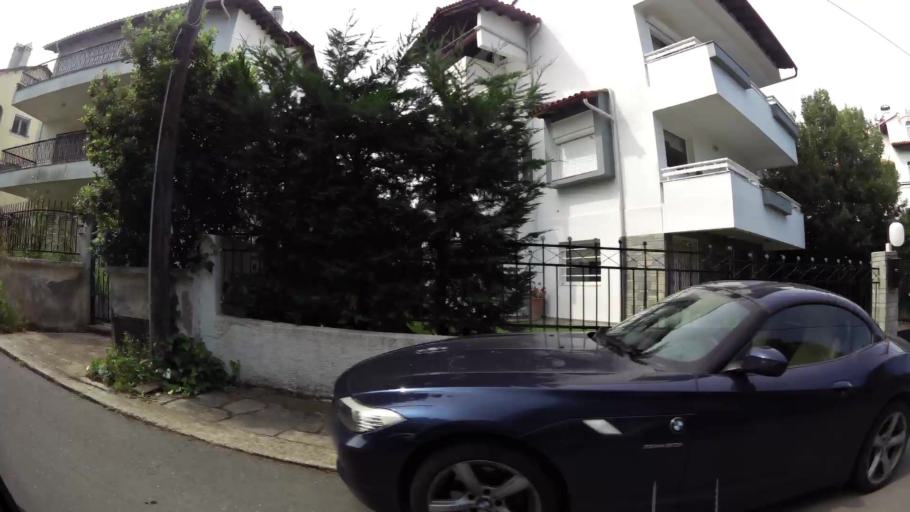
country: GR
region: Central Macedonia
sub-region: Nomos Thessalonikis
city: Panorama
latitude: 40.5825
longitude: 23.0209
